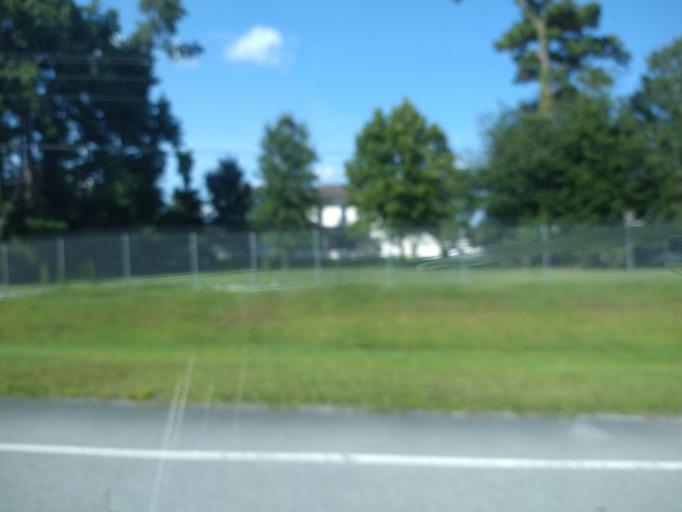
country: US
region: North Carolina
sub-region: Onslow County
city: Piney Green
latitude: 34.7307
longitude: -77.3480
